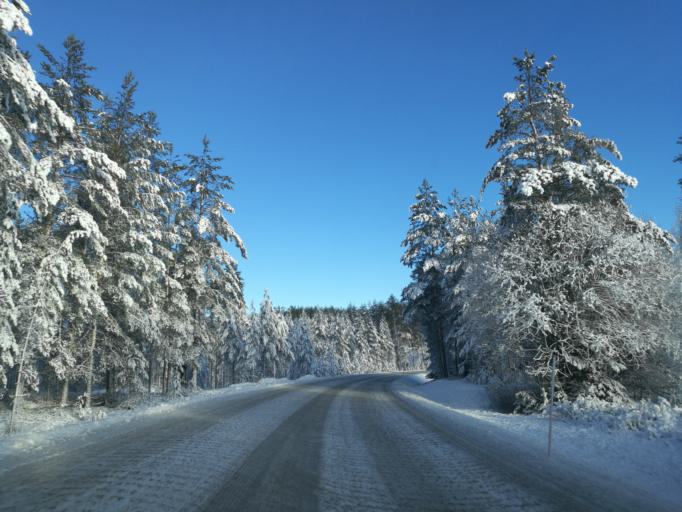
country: NO
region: Hedmark
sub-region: Grue
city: Kirkenaer
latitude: 60.4139
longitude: 12.3921
